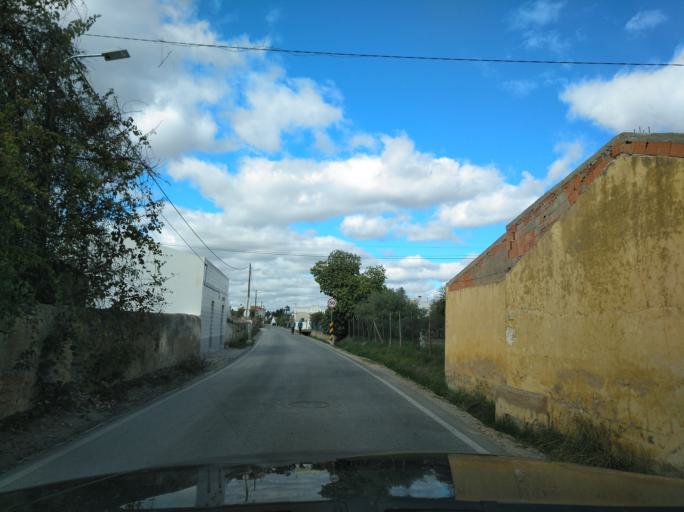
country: PT
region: Faro
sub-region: Tavira
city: Luz
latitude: 37.0951
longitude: -7.7047
